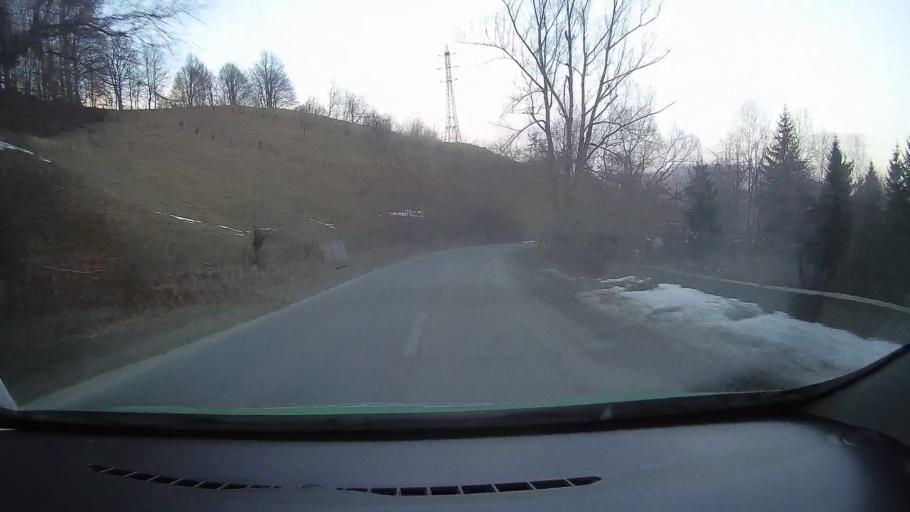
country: RO
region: Prahova
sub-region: Comuna Secaria
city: Secaria
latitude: 45.2685
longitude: 25.6758
